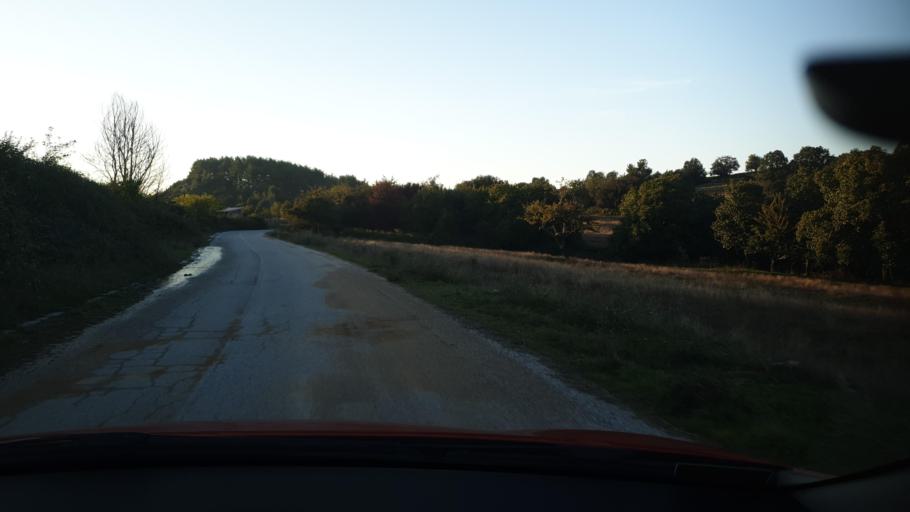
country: GR
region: Central Macedonia
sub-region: Nomos Chalkidikis
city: Galatista
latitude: 40.5077
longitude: 23.2228
